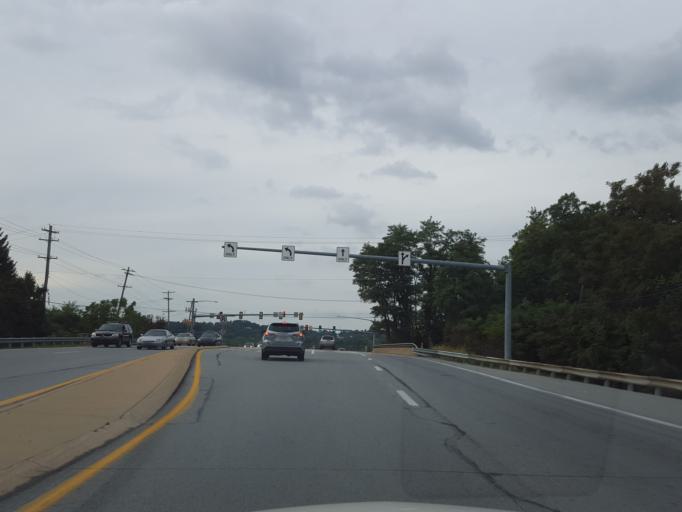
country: US
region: Pennsylvania
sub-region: York County
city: Yorklyn
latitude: 39.9825
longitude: -76.6640
